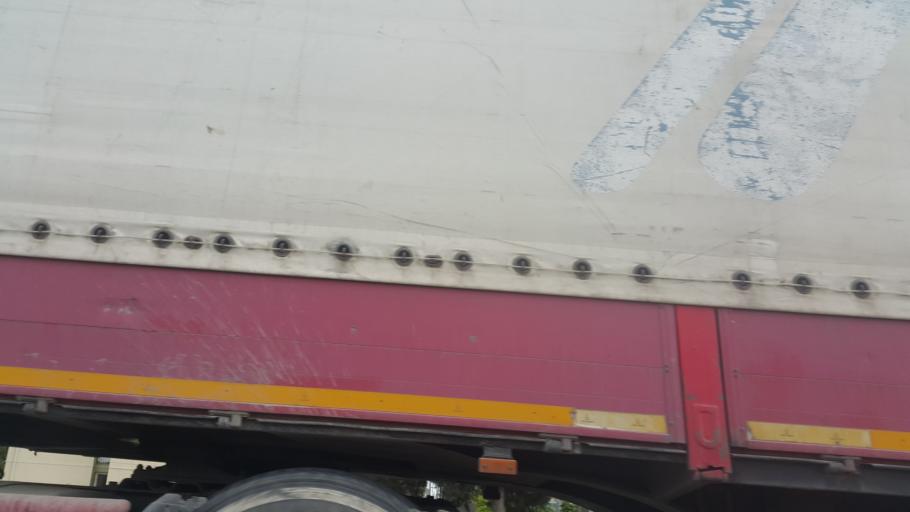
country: TR
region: Mersin
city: Yenice
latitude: 36.9734
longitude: 35.0590
